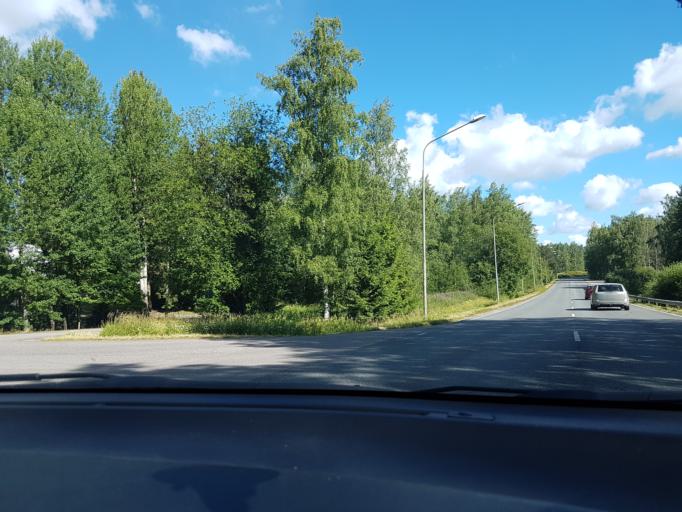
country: FI
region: Uusimaa
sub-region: Helsinki
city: Kerava
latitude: 60.3839
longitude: 25.0982
